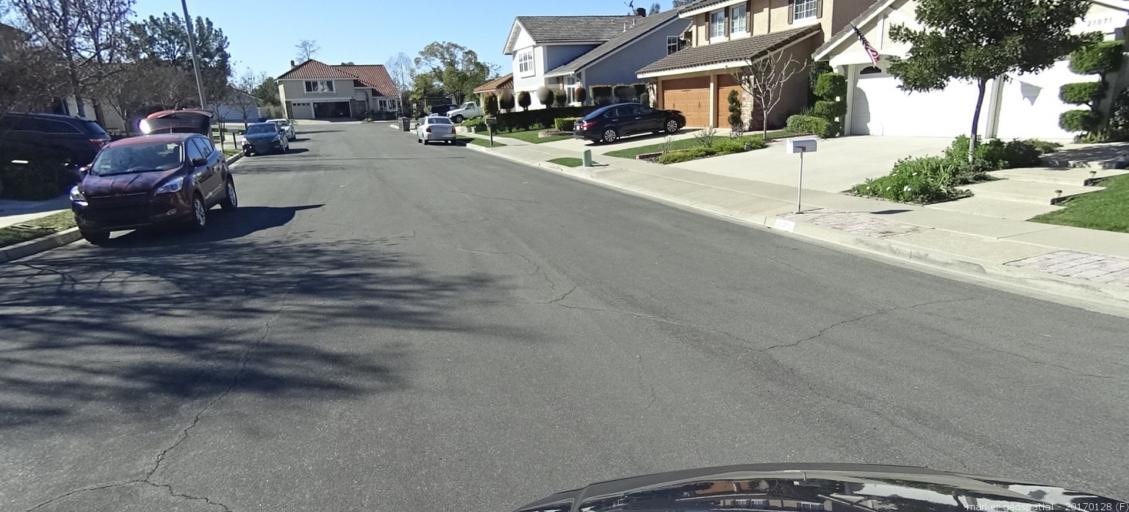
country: US
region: California
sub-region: Orange County
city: Lake Forest
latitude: 33.6568
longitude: -117.6926
